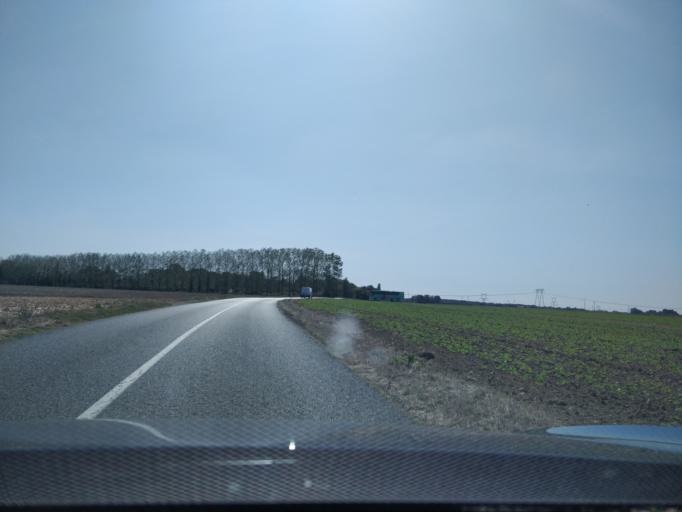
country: FR
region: Ile-de-France
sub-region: Departement de l'Essonne
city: Gometz-la-Ville
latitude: 48.6518
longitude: 2.1481
